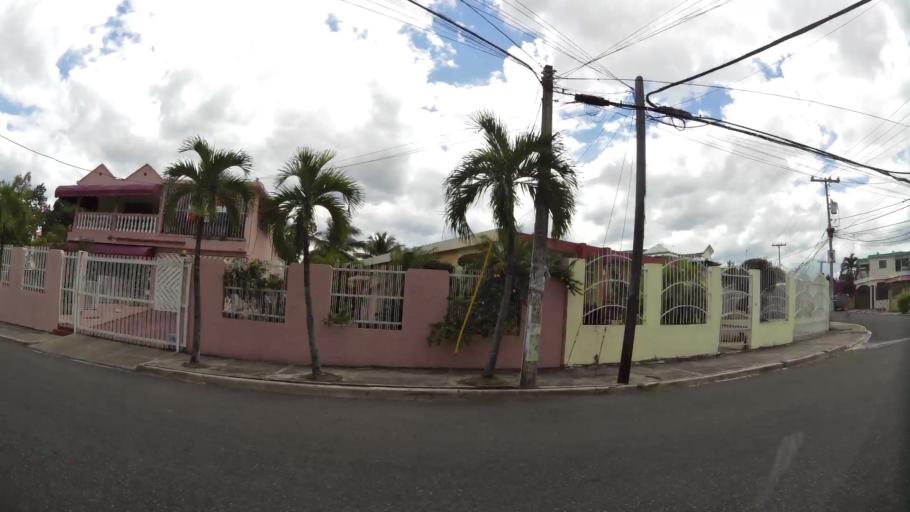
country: DO
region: Nacional
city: Ensanche Luperon
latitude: 18.5180
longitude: -69.9061
